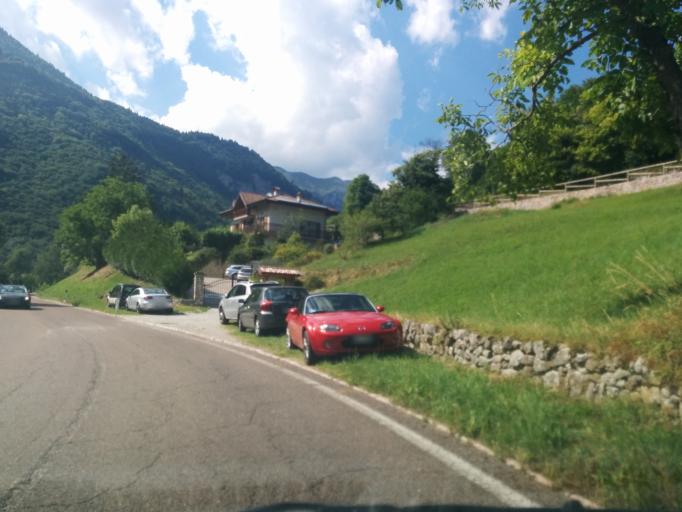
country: IT
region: Trentino-Alto Adige
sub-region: Provincia di Trento
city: Tenno
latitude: 45.9326
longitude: 10.8158
